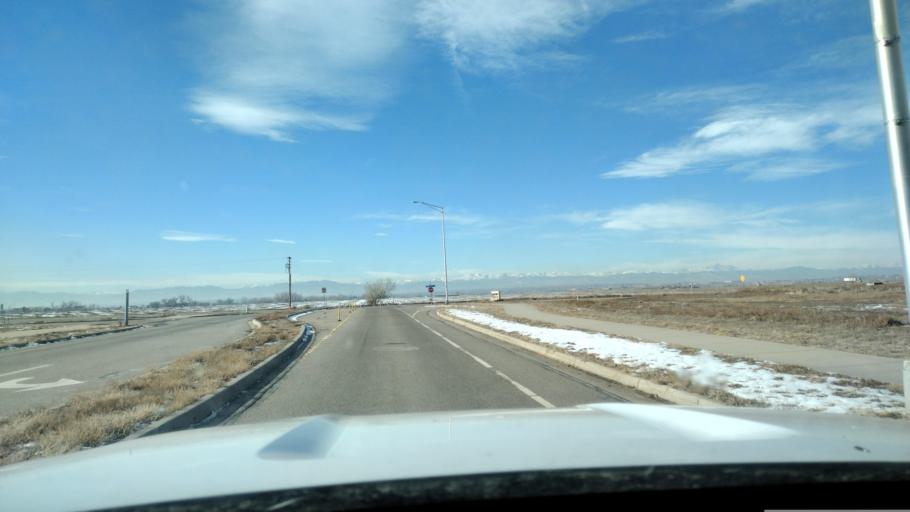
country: US
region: Colorado
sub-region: Adams County
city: Brighton
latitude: 39.9240
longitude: -104.8169
